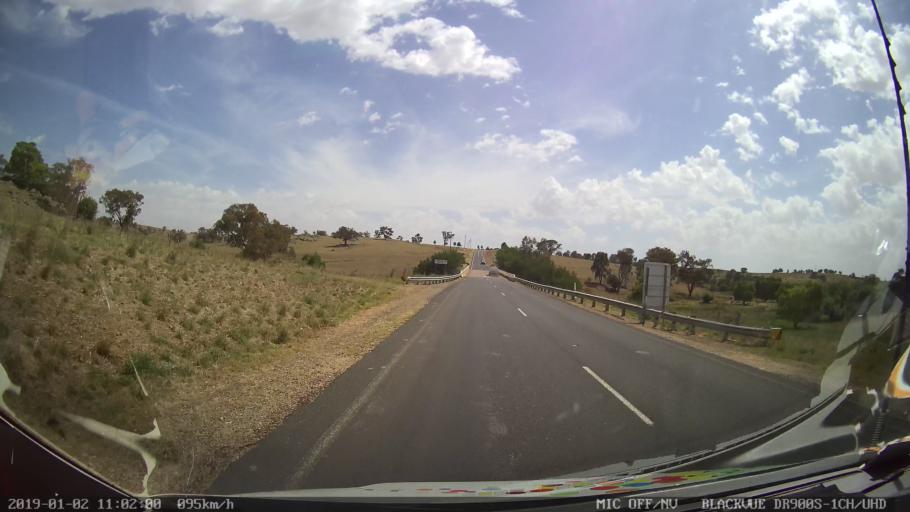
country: AU
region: New South Wales
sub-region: Young
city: Young
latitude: -34.5909
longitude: 148.3239
